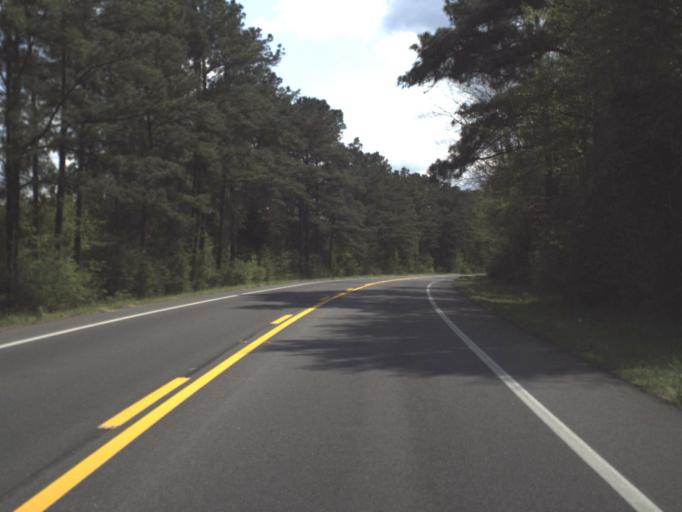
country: US
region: Florida
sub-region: Okaloosa County
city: Crestview
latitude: 30.9035
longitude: -86.4907
